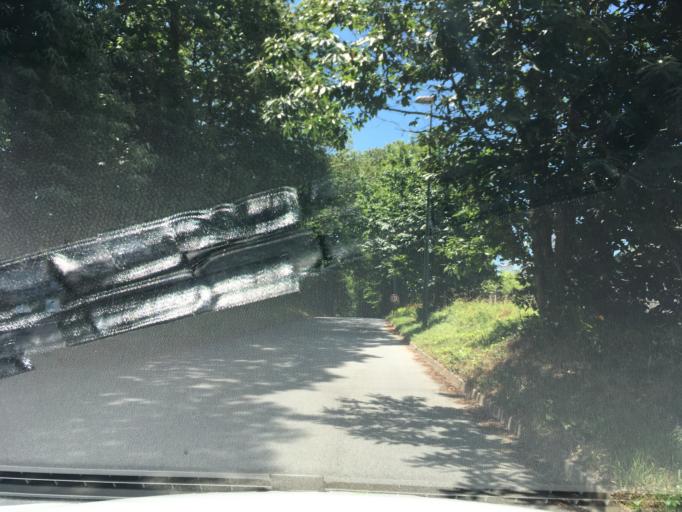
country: FR
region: Brittany
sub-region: Departement du Finistere
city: Quimper
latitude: 47.9976
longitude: -4.1328
